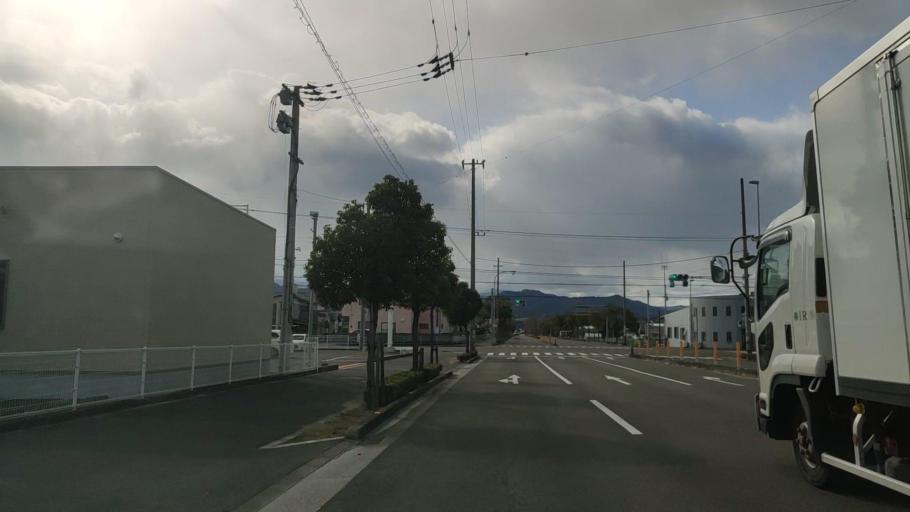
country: JP
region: Ehime
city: Saijo
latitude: 34.0417
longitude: 133.0017
